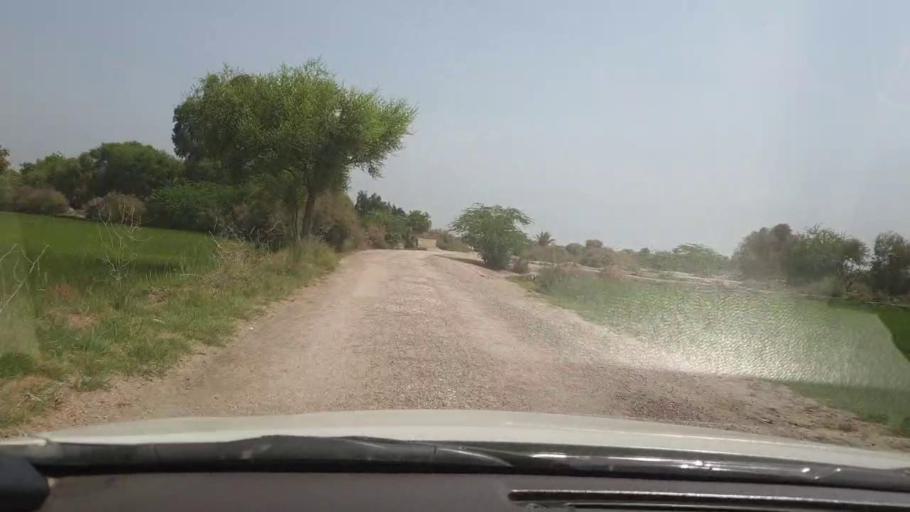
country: PK
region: Sindh
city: Shikarpur
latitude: 27.9297
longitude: 68.6042
